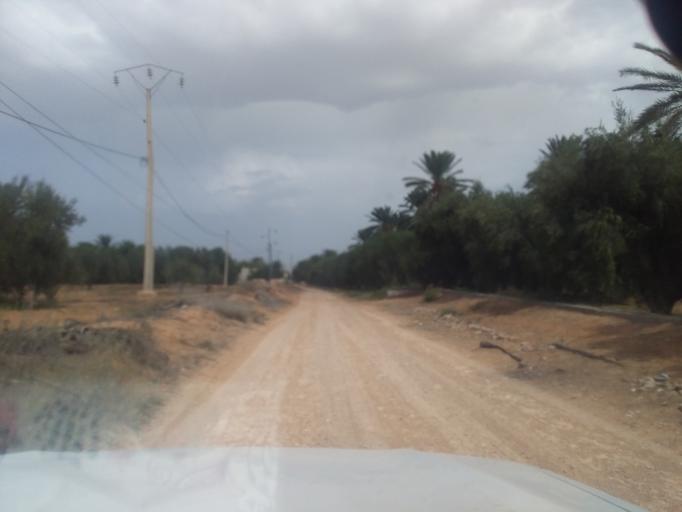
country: TN
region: Madanin
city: Medenine
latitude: 33.5975
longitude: 10.3249
